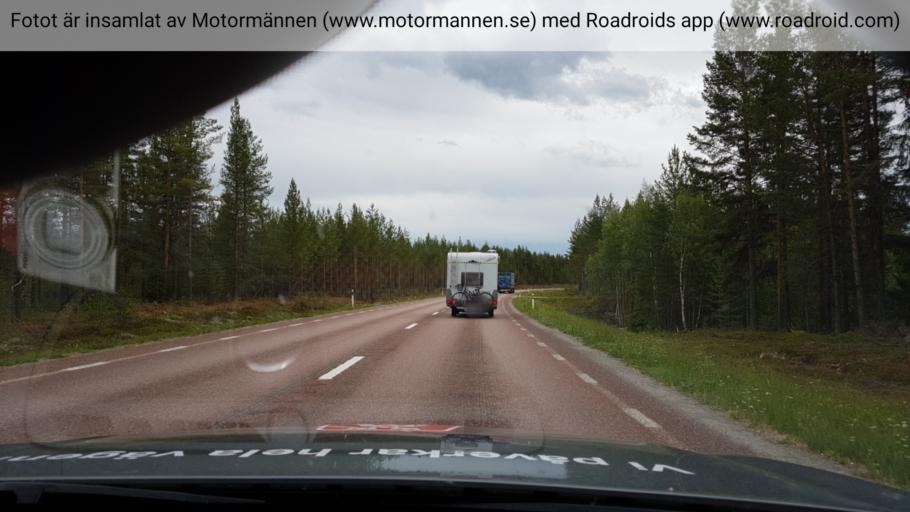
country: SE
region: Jaemtland
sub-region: Bergs Kommun
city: Hoverberg
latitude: 62.6139
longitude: 14.3931
